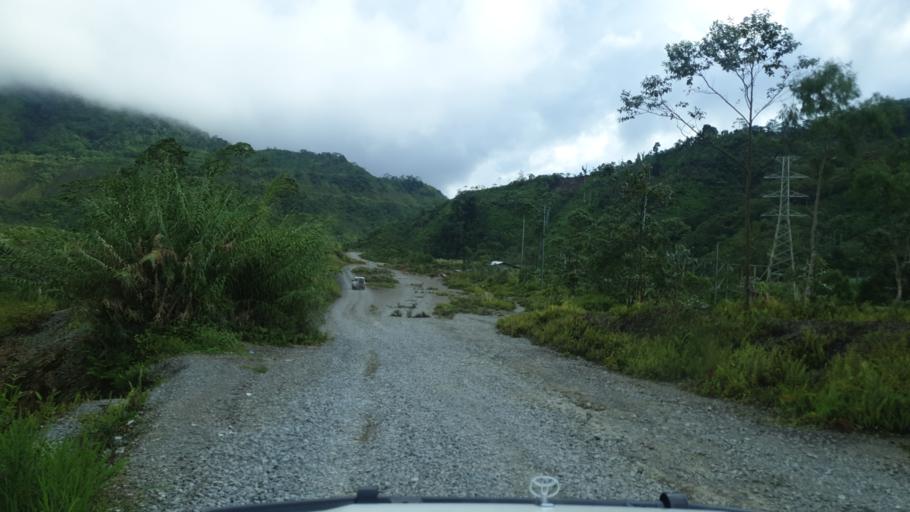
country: PG
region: Bougainville
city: Panguna
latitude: -6.3103
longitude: 155.4877
